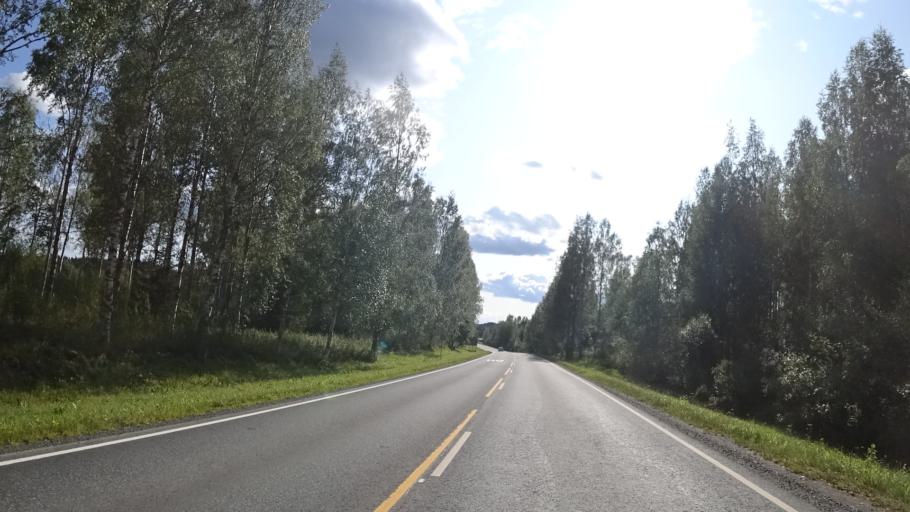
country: FI
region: North Karelia
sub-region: Keski-Karjala
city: Tohmajaervi
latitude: 62.2282
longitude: 30.3179
